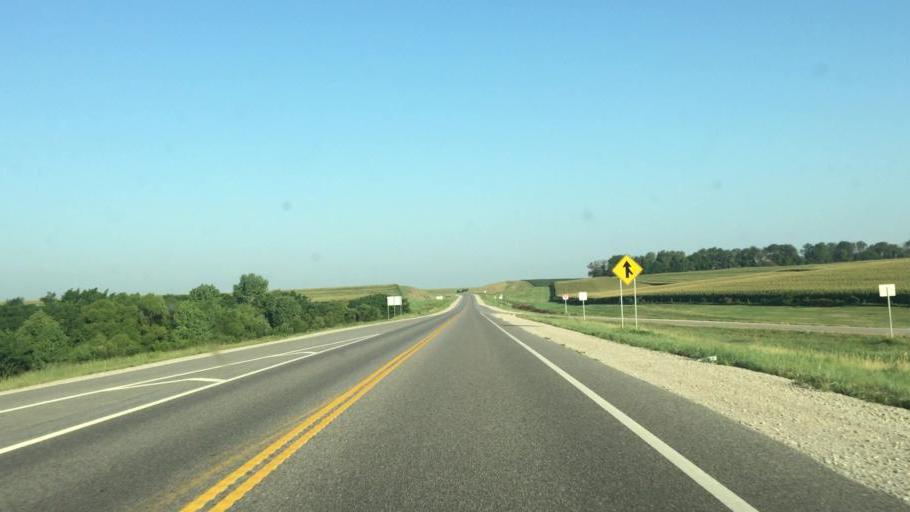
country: US
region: Kansas
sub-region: Doniphan County
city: Highland
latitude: 39.8403
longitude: -95.2679
